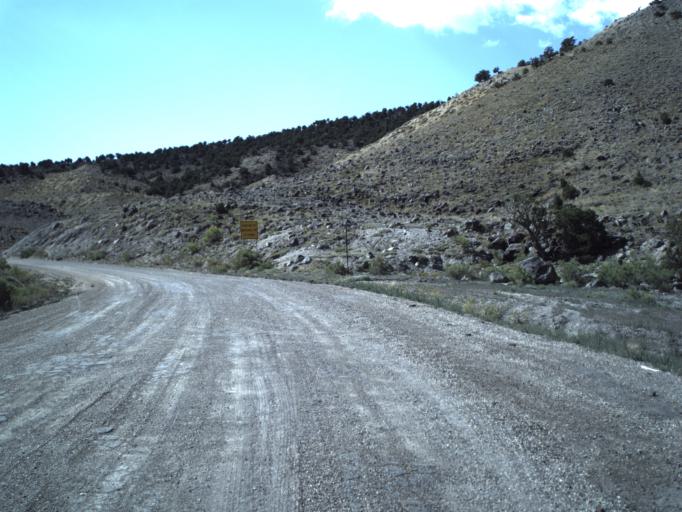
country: US
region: Utah
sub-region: Emery County
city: Ferron
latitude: 38.7643
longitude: -111.3497
